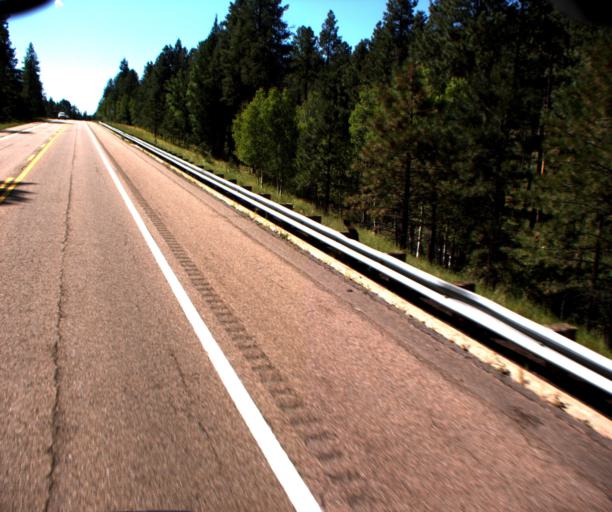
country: US
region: Arizona
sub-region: Apache County
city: Eagar
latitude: 33.9013
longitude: -109.1591
